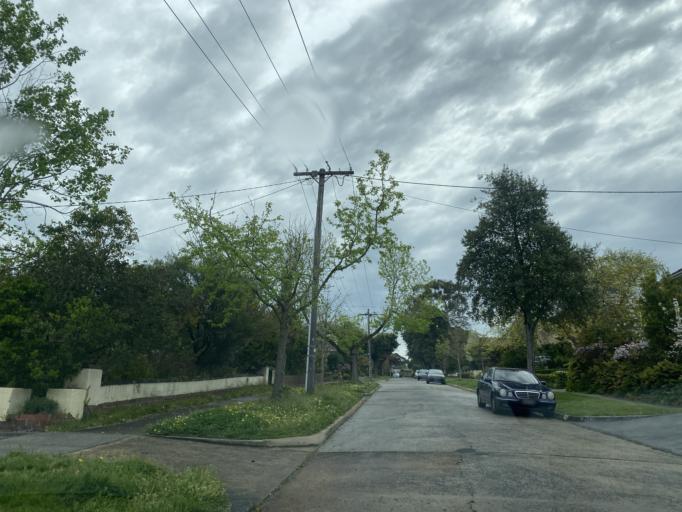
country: AU
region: Victoria
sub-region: Boroondara
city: Camberwell
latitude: -37.8381
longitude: 145.0687
